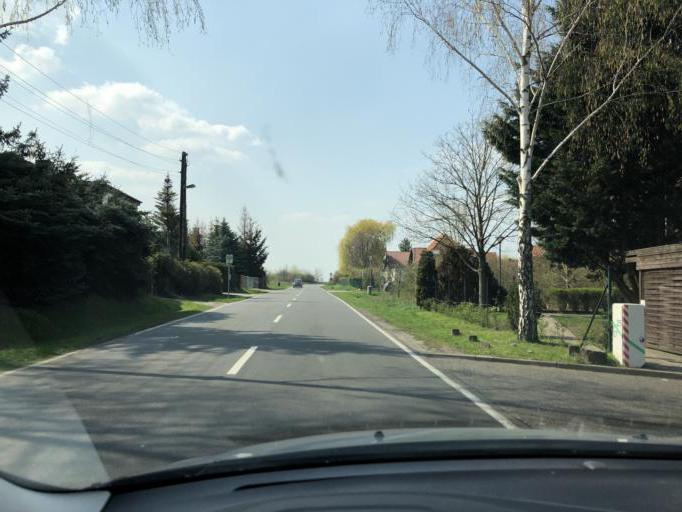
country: DE
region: Saxony-Anhalt
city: Zorbig
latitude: 51.6236
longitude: 12.1070
